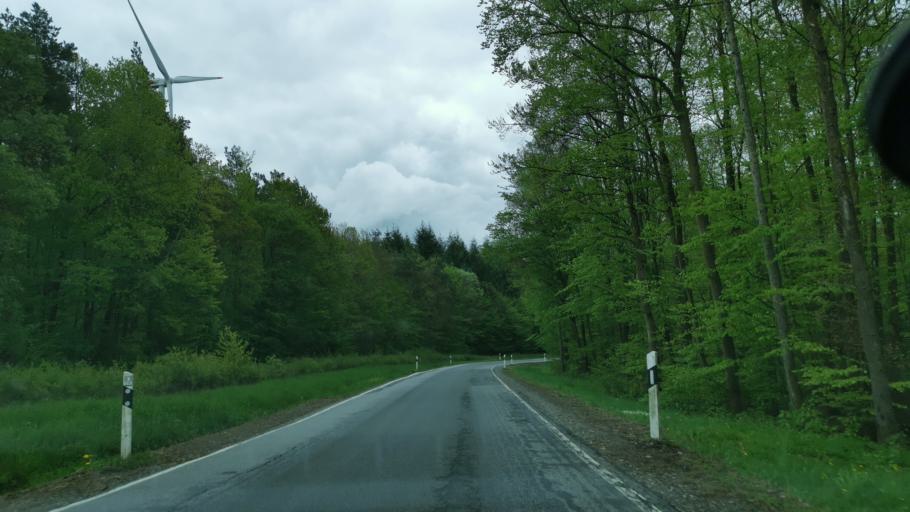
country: DE
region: Baden-Wuerttemberg
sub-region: Karlsruhe Region
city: Walldurn
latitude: 49.5345
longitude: 9.3942
